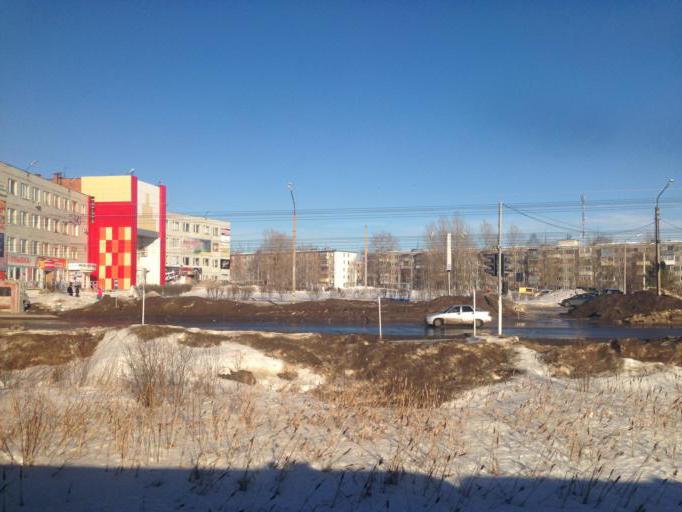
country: RU
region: Komi Republic
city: Ezhva
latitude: 61.7980
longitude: 50.7362
